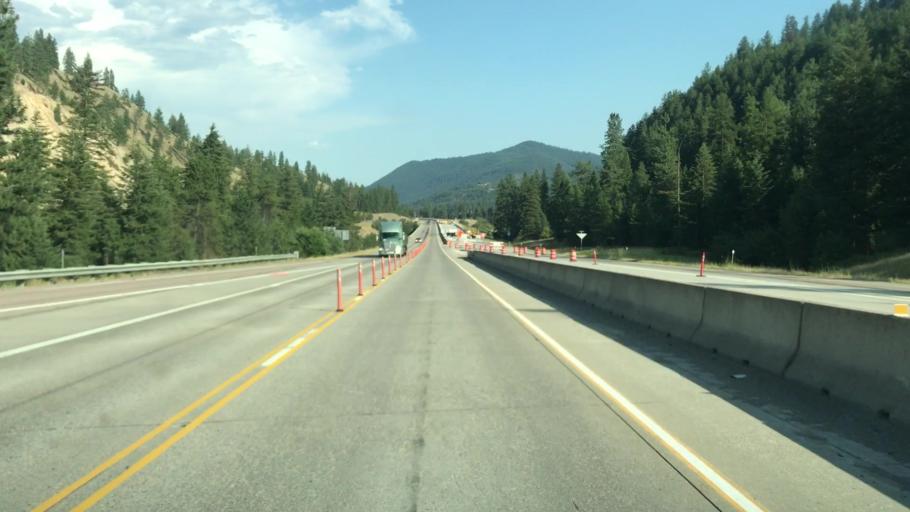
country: US
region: Montana
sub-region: Mineral County
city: Superior
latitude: 47.2238
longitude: -114.9656
